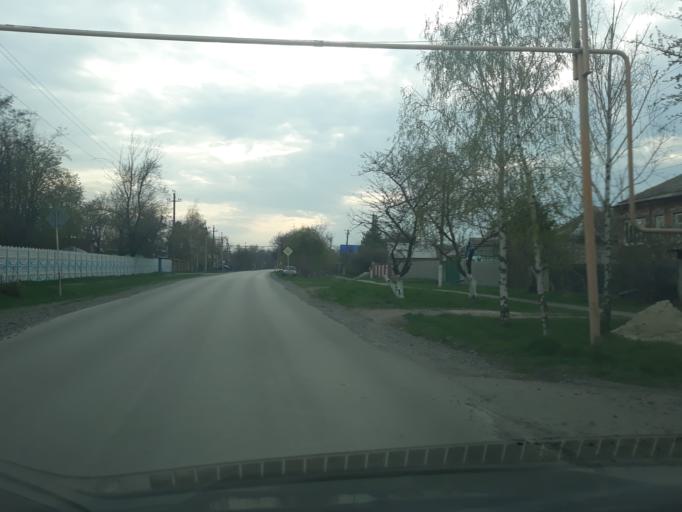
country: RU
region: Rostov
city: Novobessergenovka
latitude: 47.1619
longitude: 38.7232
